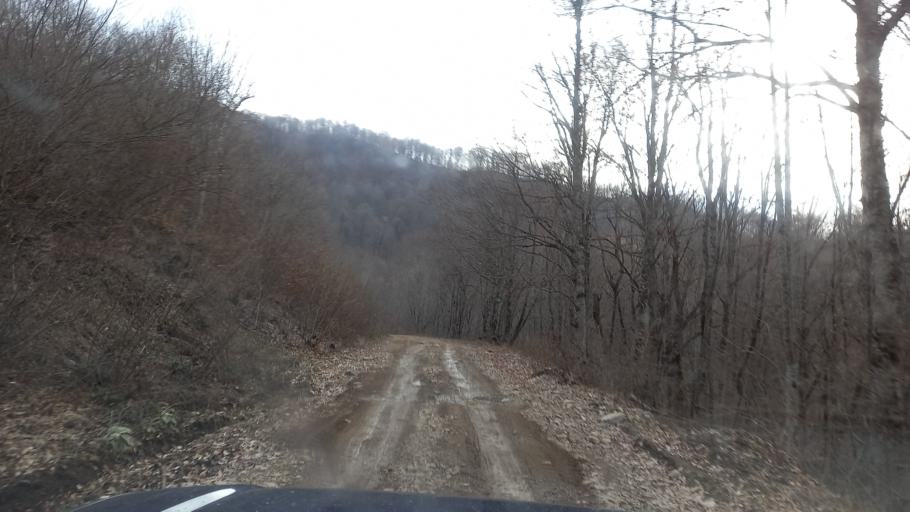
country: RU
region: Adygeya
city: Kamennomostskiy
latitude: 44.1568
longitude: 40.3017
